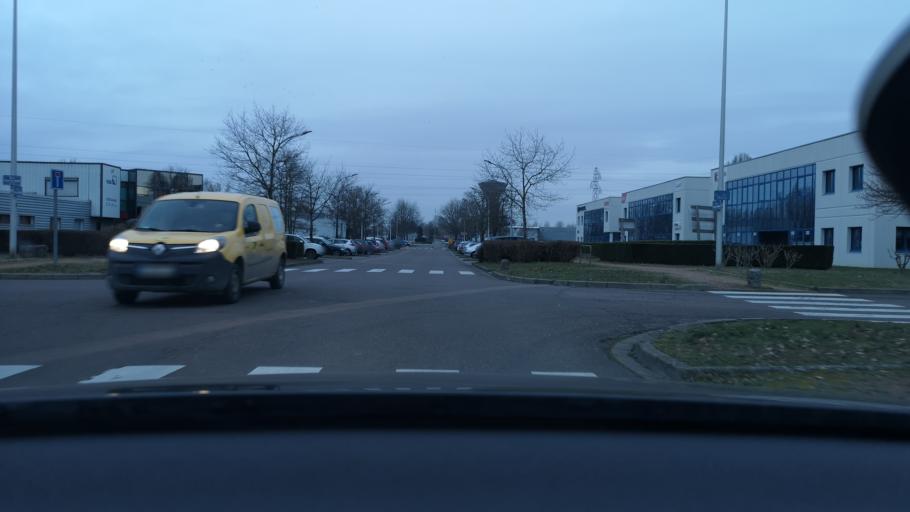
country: FR
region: Bourgogne
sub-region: Departement de Saone-et-Loire
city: Chalon-sur-Saone
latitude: 46.7667
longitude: 4.8578
